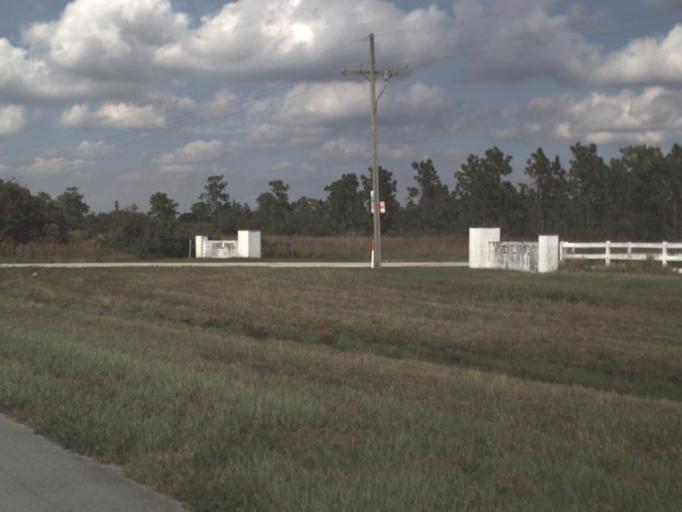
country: US
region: Florida
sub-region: Indian River County
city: Fellsmere
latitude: 27.6052
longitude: -80.8512
